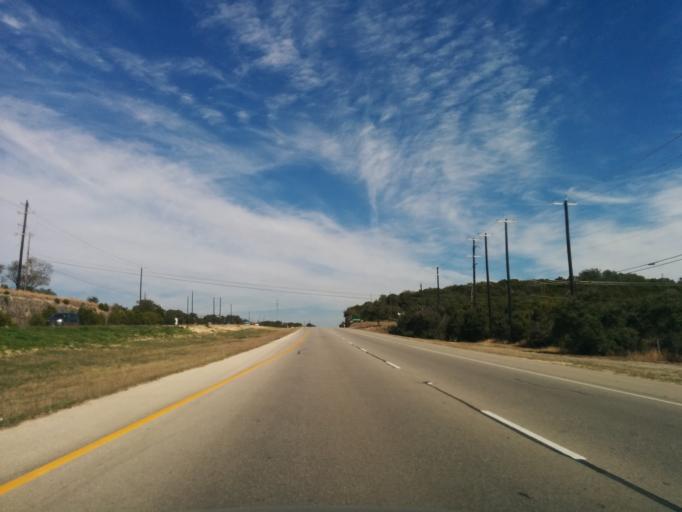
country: US
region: Texas
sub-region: Comal County
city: Bulverde
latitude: 29.7711
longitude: -98.4274
